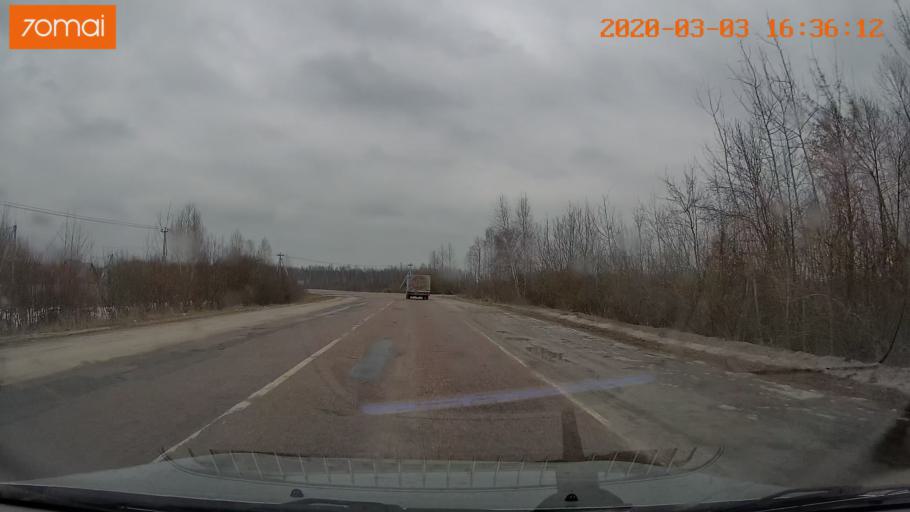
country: RU
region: Moskovskaya
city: Lopatinskiy
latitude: 55.4001
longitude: 38.7697
